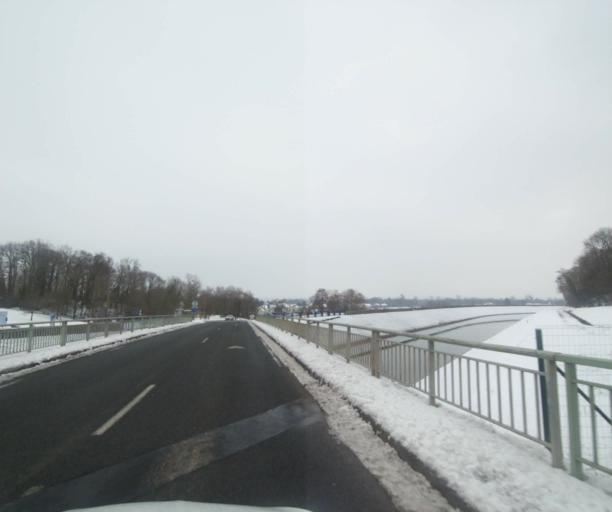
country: FR
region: Champagne-Ardenne
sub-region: Departement de la Haute-Marne
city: Villiers-en-Lieu
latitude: 48.6158
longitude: 4.8903
